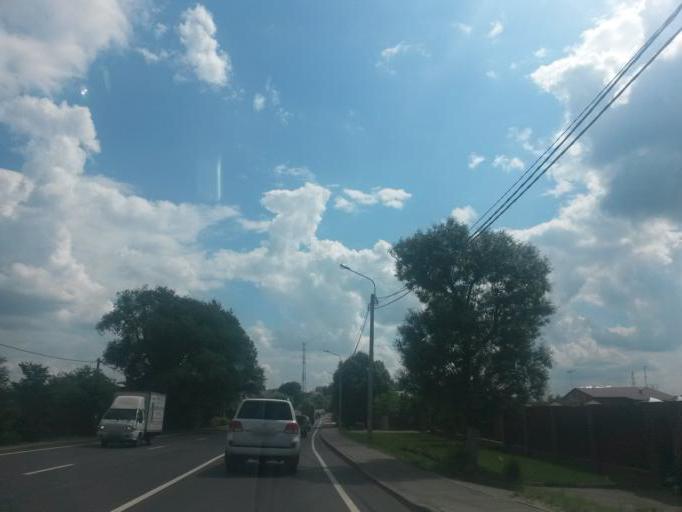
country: RU
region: Moskovskaya
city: Vostryakovo
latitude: 55.3933
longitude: 37.7885
